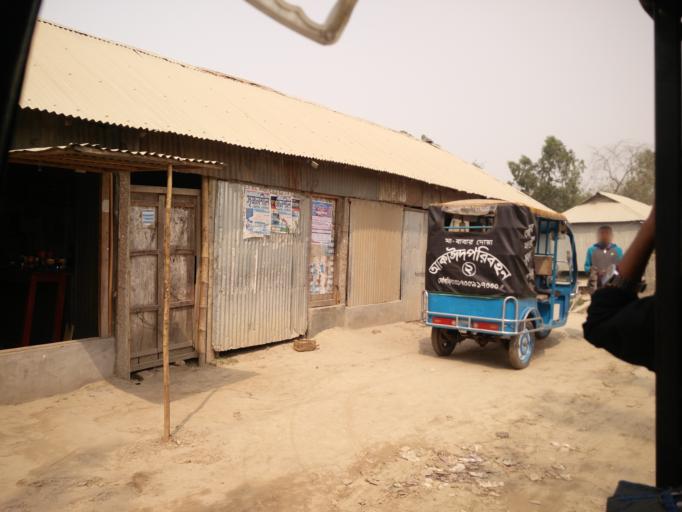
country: BD
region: Rangpur Division
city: Nageswari
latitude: 25.8887
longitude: 89.7073
